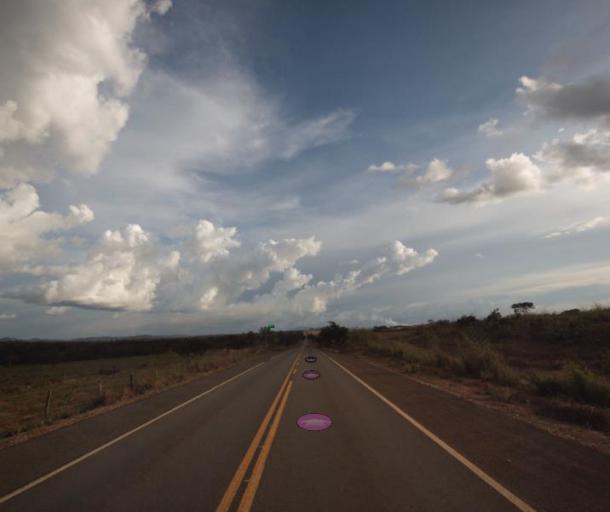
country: BR
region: Goias
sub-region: Niquelandia
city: Niquelandia
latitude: -14.7233
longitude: -48.6094
